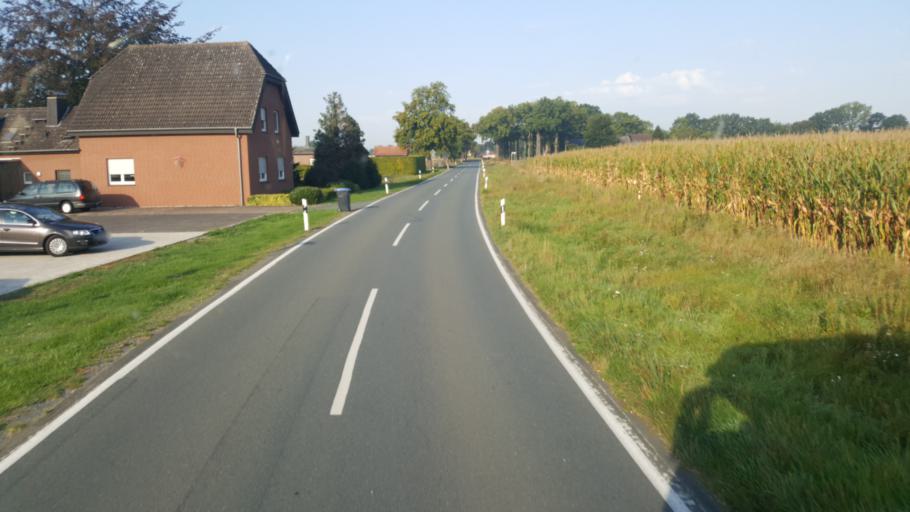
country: DE
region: North Rhine-Westphalia
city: Rietberg
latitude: 51.7380
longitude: 8.4034
